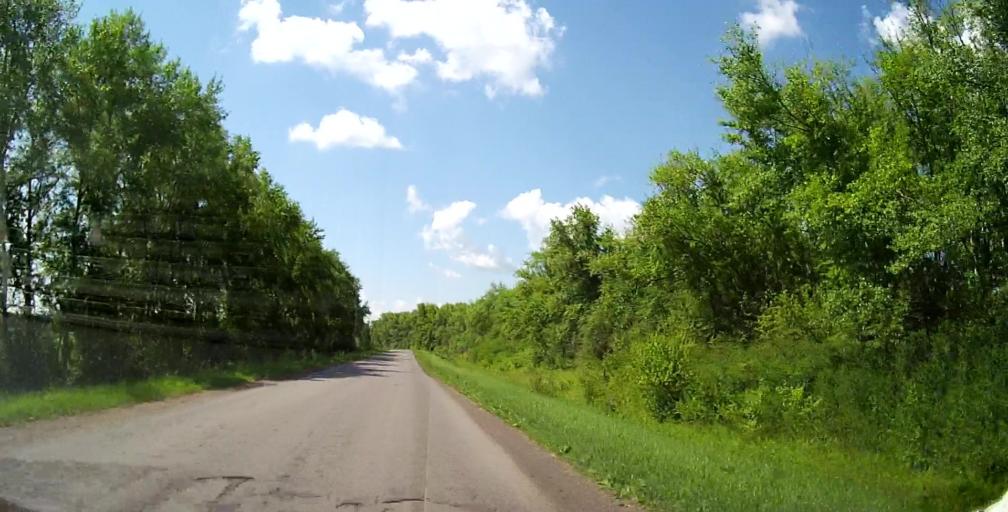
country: RU
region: Lipetsk
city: Chaplygin
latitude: 53.3090
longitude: 39.9547
